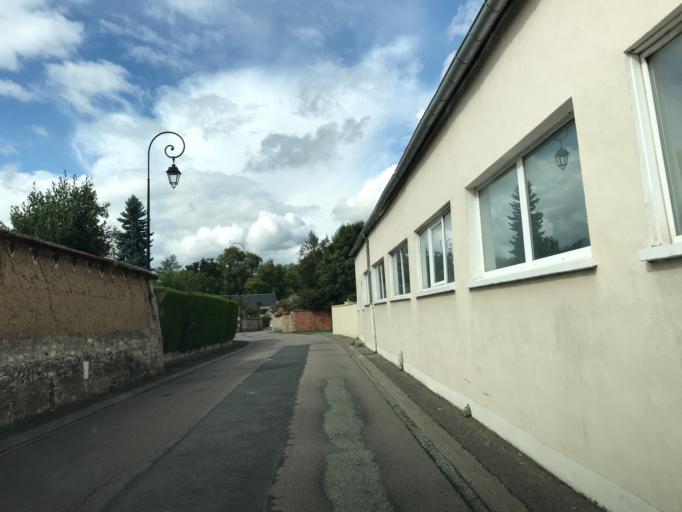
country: FR
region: Haute-Normandie
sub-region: Departement de l'Eure
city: Saint-Just
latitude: 49.1062
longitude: 1.4417
